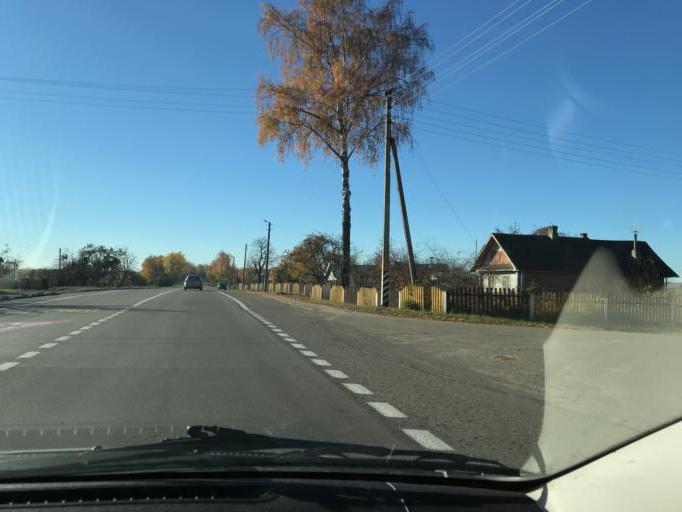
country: BY
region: Vitebsk
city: Lyepyel'
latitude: 54.9324
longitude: 28.7589
